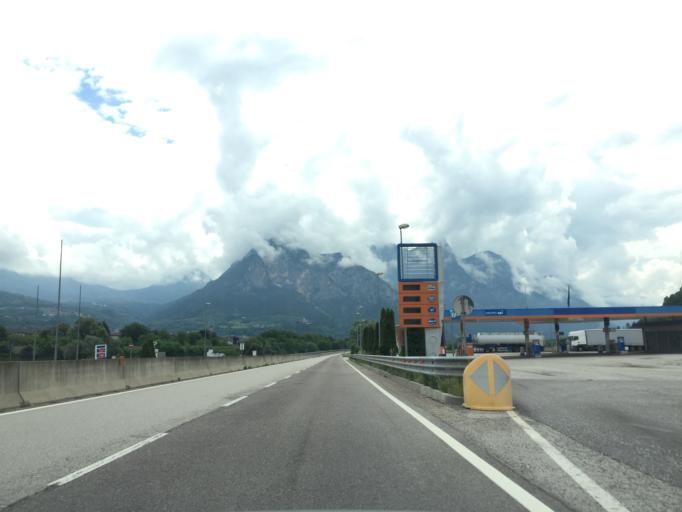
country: IT
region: Trentino-Alto Adige
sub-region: Provincia di Trento
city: Castelnuovo
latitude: 46.0510
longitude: 11.4840
